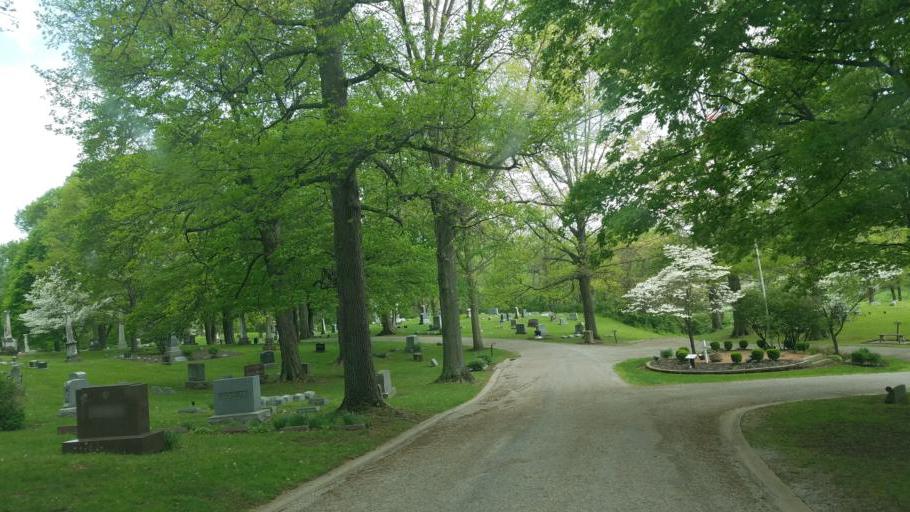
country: US
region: Ohio
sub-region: Licking County
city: Granville
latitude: 40.0646
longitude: -82.5141
